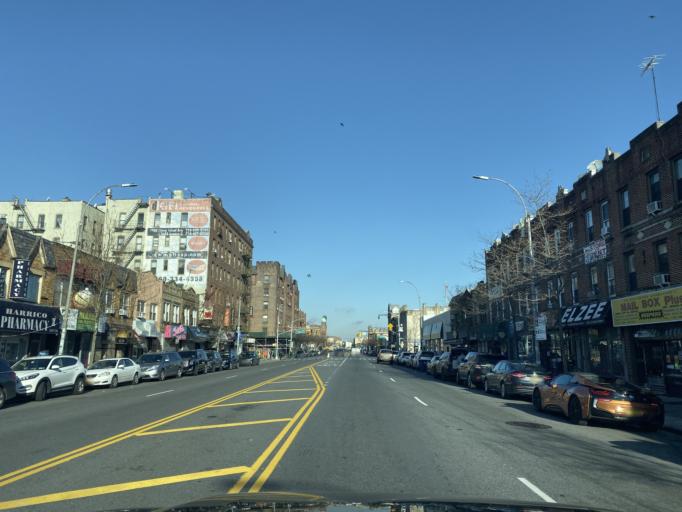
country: US
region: New York
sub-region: Kings County
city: Brooklyn
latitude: 40.6241
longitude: -73.9650
